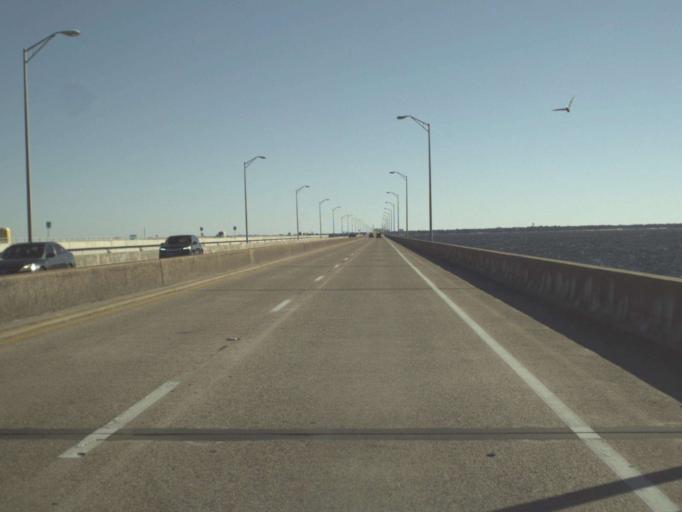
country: US
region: Florida
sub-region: Escambia County
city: East Pensacola Heights
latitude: 30.4132
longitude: -87.1920
